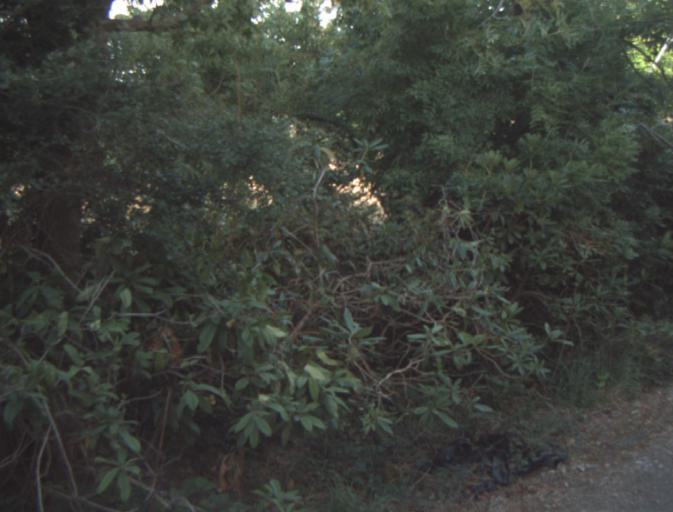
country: AU
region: Tasmania
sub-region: Launceston
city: Mayfield
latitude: -41.2730
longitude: 147.1834
